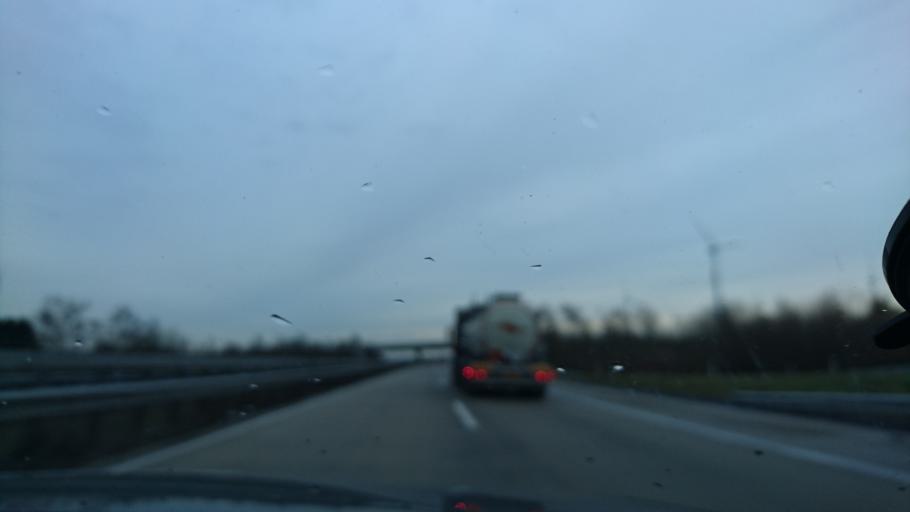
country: NL
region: Overijssel
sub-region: Gemeente Losser
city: Losser
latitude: 52.3231
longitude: 7.0640
